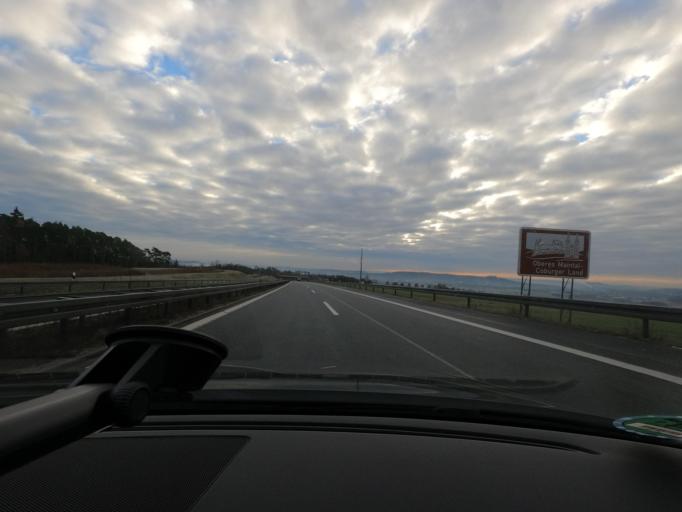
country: DE
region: Bavaria
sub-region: Upper Franconia
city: Lautertal
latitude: 50.3230
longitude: 10.9475
